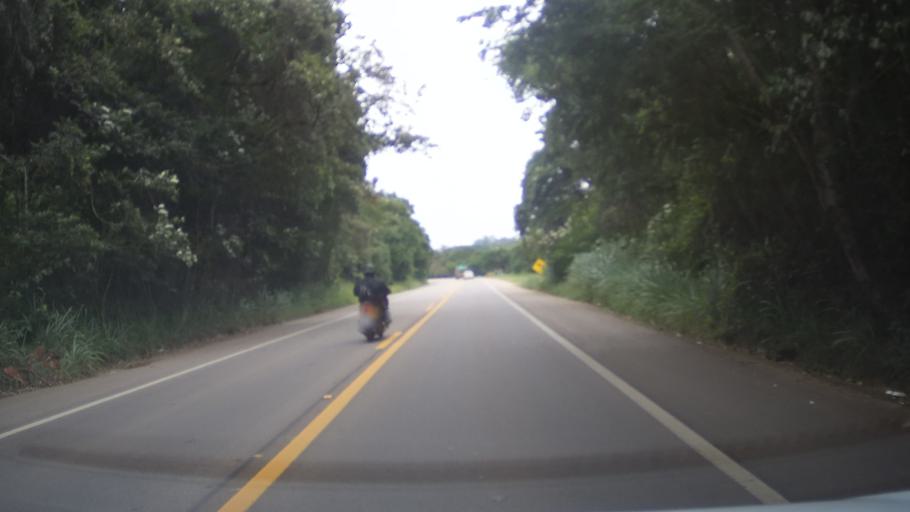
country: BR
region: Sao Paulo
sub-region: Louveira
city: Louveira
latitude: -23.0574
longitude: -46.9520
